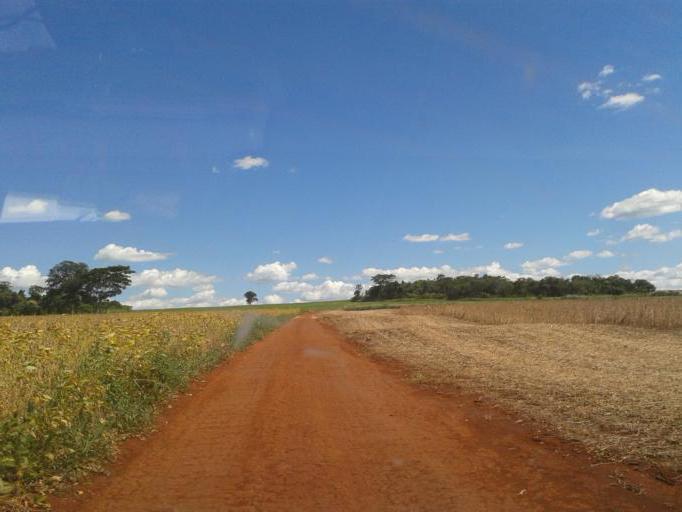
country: BR
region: Minas Gerais
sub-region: Capinopolis
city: Capinopolis
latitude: -18.6567
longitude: -49.5673
